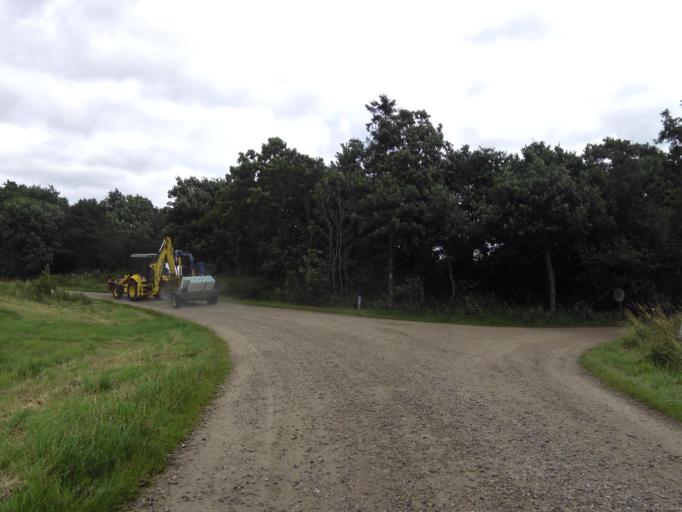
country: DK
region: South Denmark
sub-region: Haderslev Kommune
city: Gram
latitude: 55.2977
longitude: 9.1748
